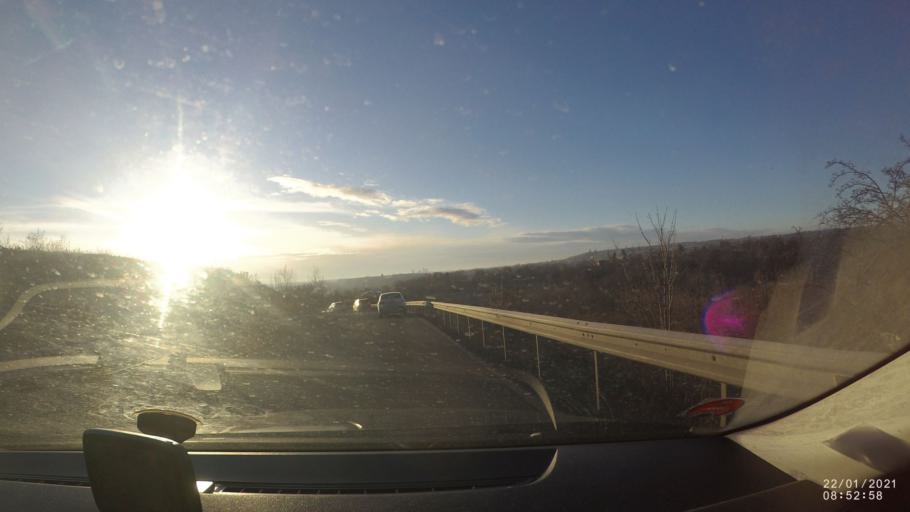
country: CZ
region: Praha
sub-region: Praha 1
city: Mala Strana
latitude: 50.1223
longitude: 14.4092
